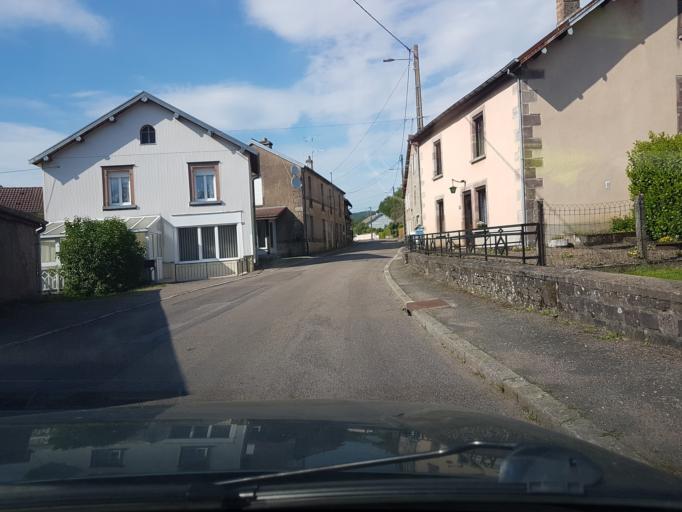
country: FR
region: Franche-Comte
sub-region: Departement de la Haute-Saone
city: Froideconche
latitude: 47.8441
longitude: 6.4739
